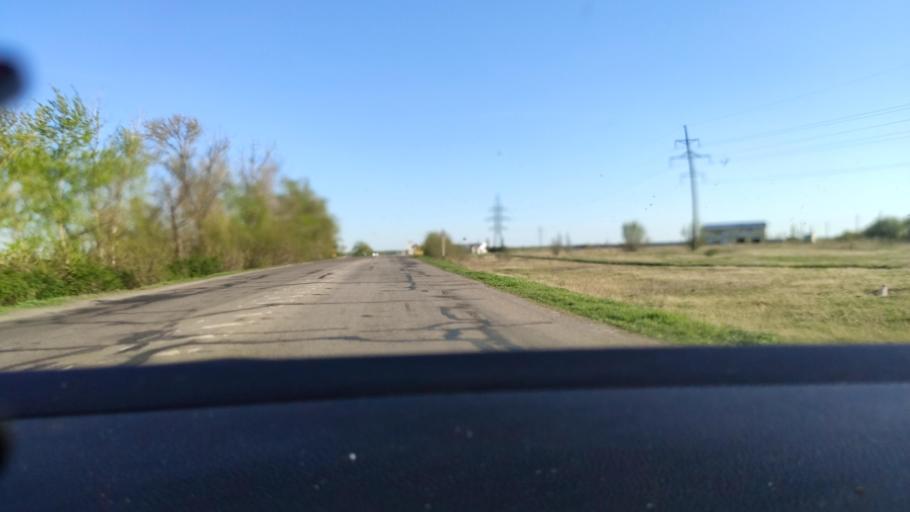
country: RU
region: Voronezj
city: Maslovka
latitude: 51.5105
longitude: 39.3042
